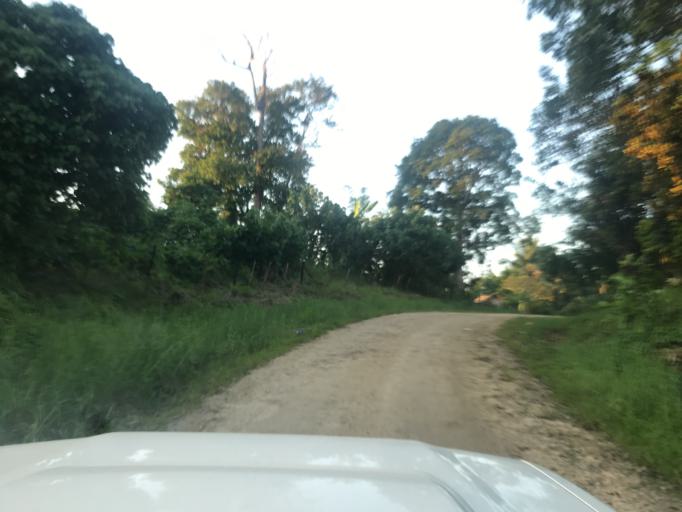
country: VU
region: Sanma
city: Luganville
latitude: -15.5700
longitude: 166.9563
